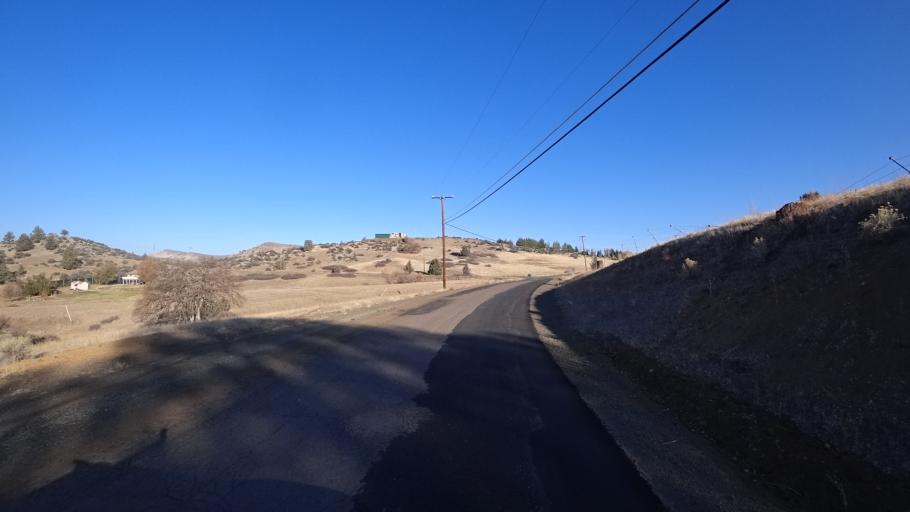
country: US
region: California
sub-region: Siskiyou County
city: Montague
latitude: 41.8915
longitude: -122.4813
